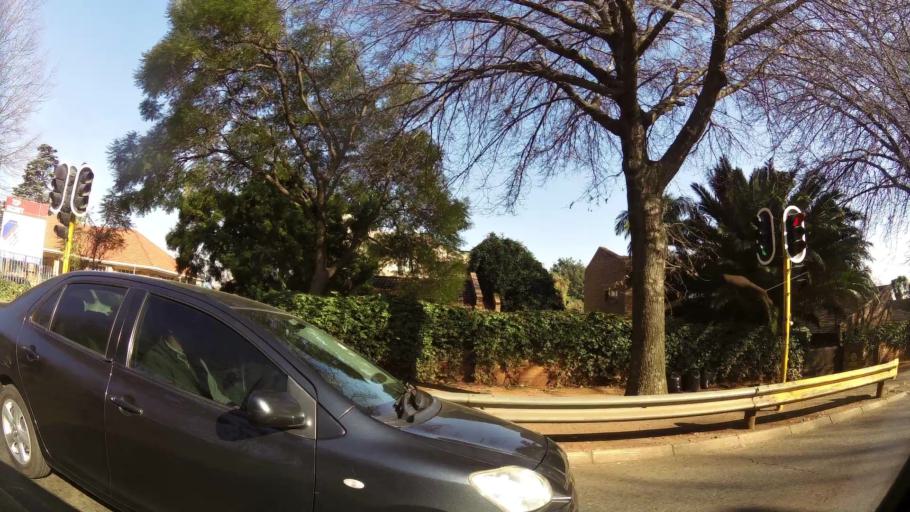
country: ZA
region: Gauteng
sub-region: Ekurhuleni Metropolitan Municipality
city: Germiston
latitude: -26.1865
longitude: 28.1360
